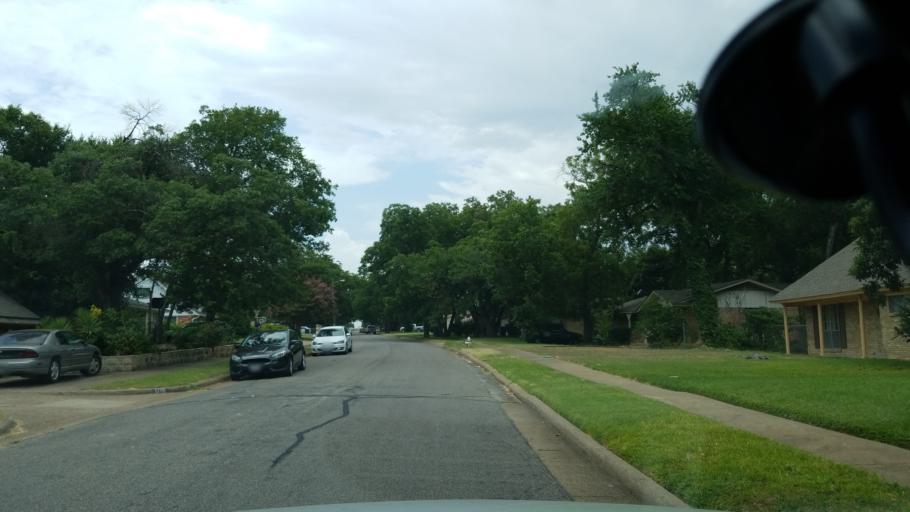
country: US
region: Texas
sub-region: Dallas County
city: Cockrell Hill
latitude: 32.6920
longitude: -96.8492
